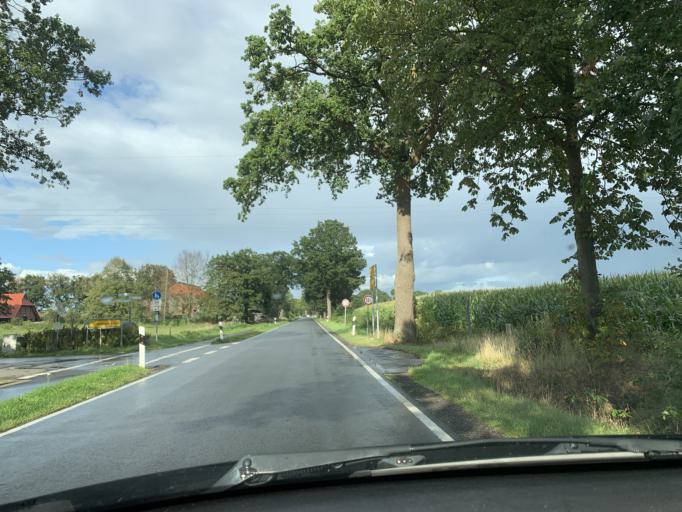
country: DE
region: Lower Saxony
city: Bockhorn
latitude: 53.3117
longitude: 8.0080
